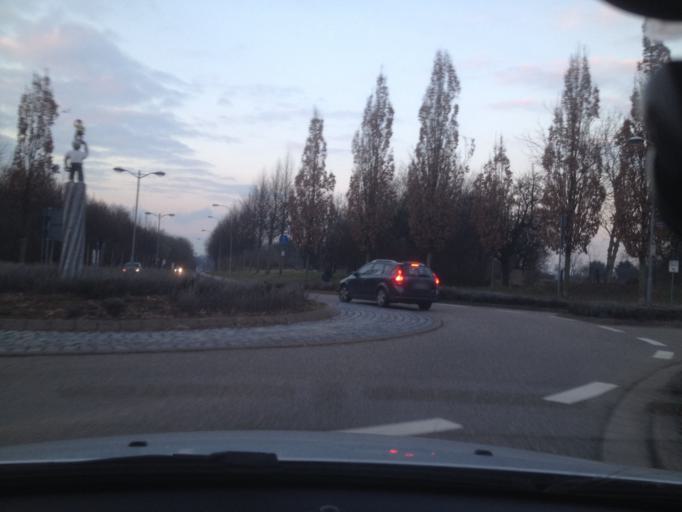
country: DE
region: Baden-Wuerttemberg
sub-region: Karlsruhe Region
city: Ettlingen
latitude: 48.9494
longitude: 8.4069
